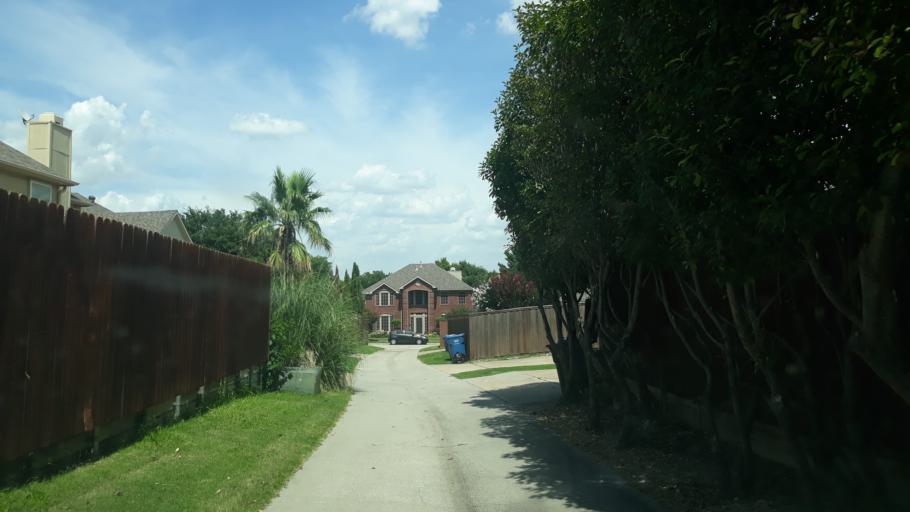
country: US
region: Texas
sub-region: Dallas County
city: Coppell
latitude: 32.9701
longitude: -97.0126
